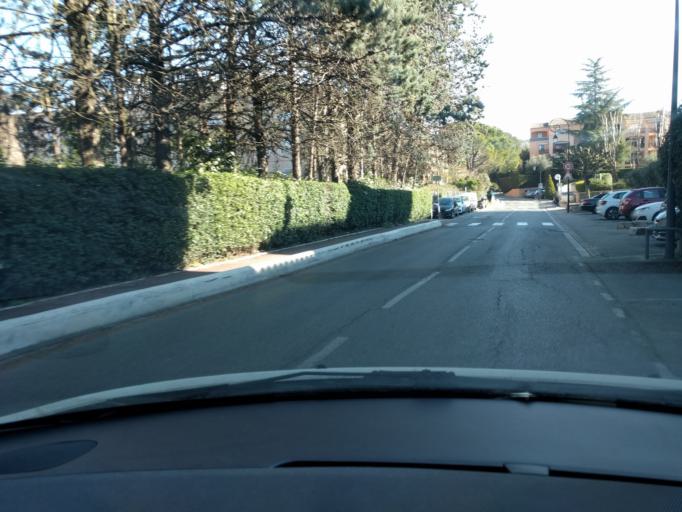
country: FR
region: Provence-Alpes-Cote d'Azur
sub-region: Departement des Alpes-Maritimes
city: Mougins
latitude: 43.6027
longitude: 6.9883
